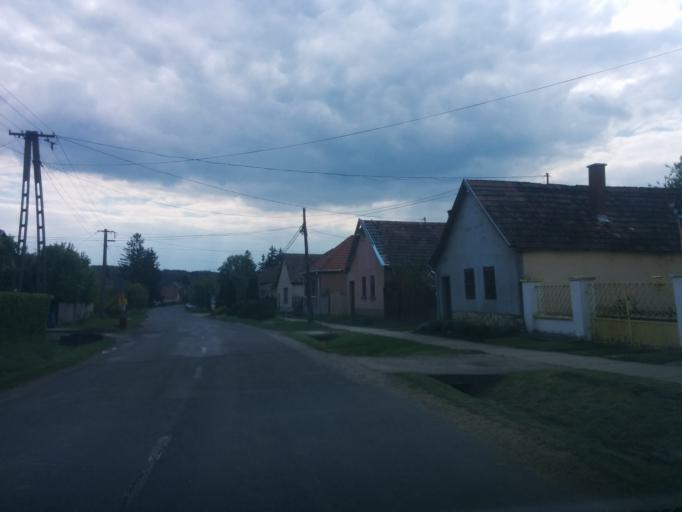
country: HU
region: Nograd
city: Romhany
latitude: 47.8442
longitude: 19.3033
